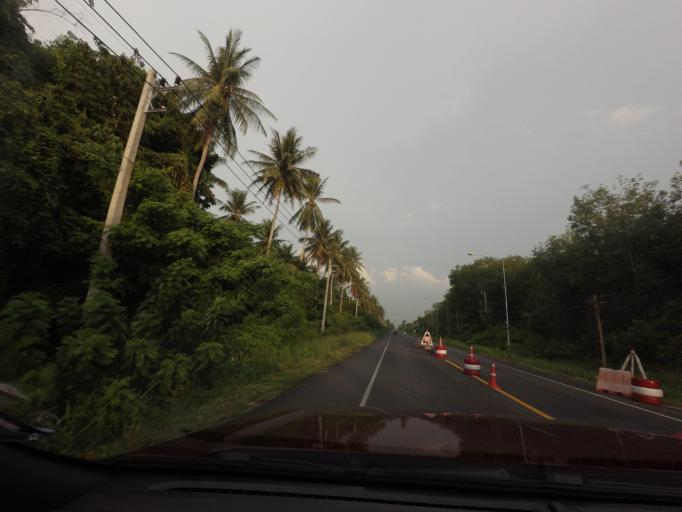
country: TH
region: Pattani
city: Mae Lan
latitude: 6.6624
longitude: 101.1666
